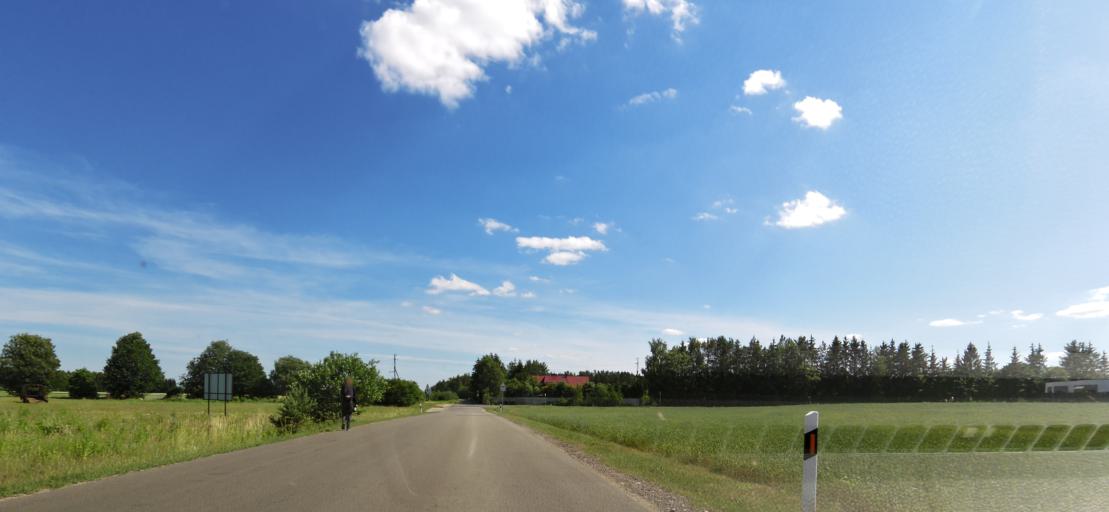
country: LT
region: Vilnius County
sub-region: Vilnius
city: Fabijoniskes
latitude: 54.8073
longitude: 25.3265
